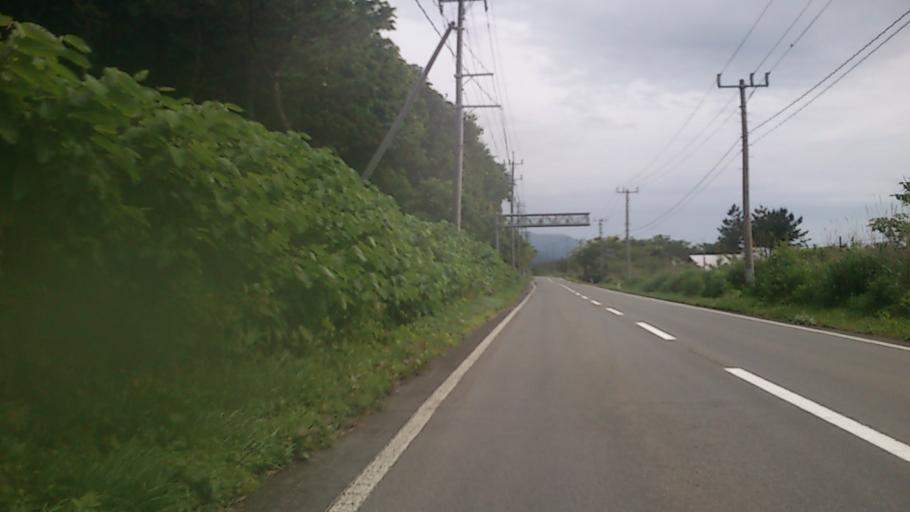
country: JP
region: Akita
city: Noshiromachi
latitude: 40.5342
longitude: 139.9478
